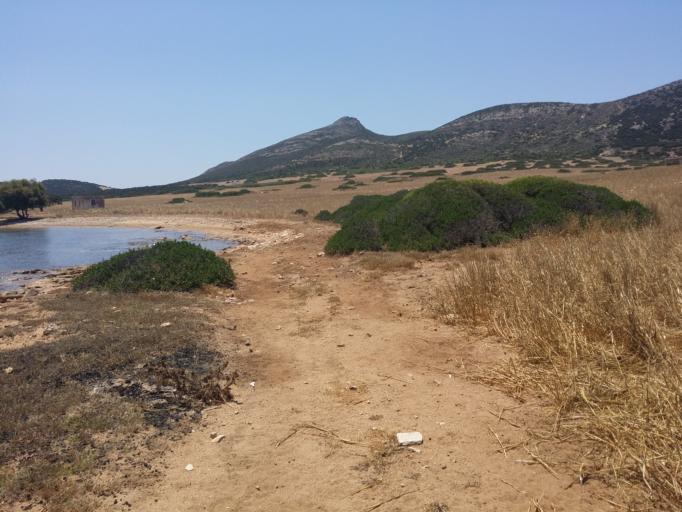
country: GR
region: South Aegean
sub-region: Nomos Kykladon
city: Antiparos
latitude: 36.9725
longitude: 25.0169
